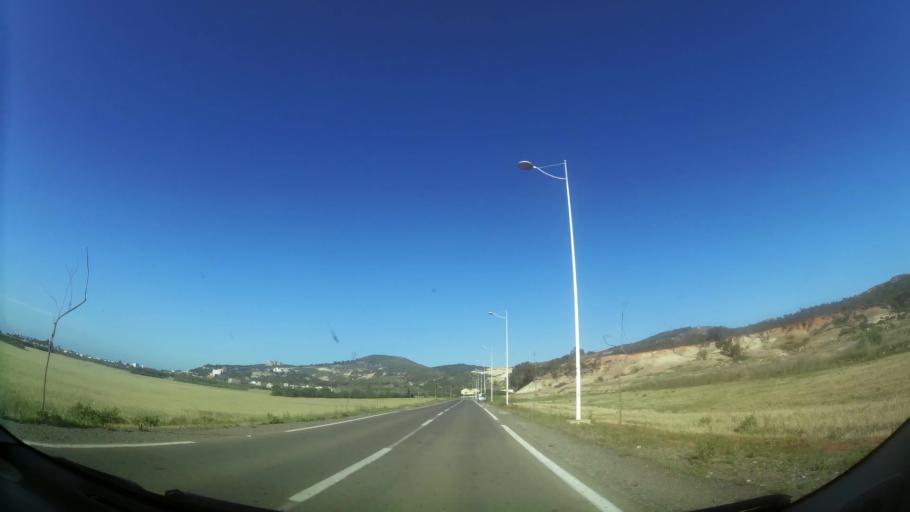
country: MA
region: Oriental
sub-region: Berkane-Taourirt
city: Madagh
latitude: 35.0649
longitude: -2.2230
